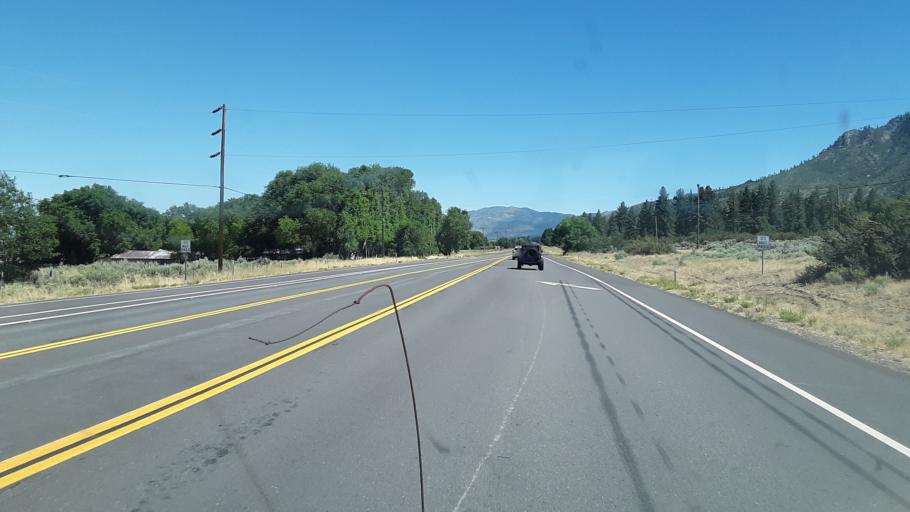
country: US
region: California
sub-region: Lassen County
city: Janesville
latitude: 40.2466
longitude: -120.4586
